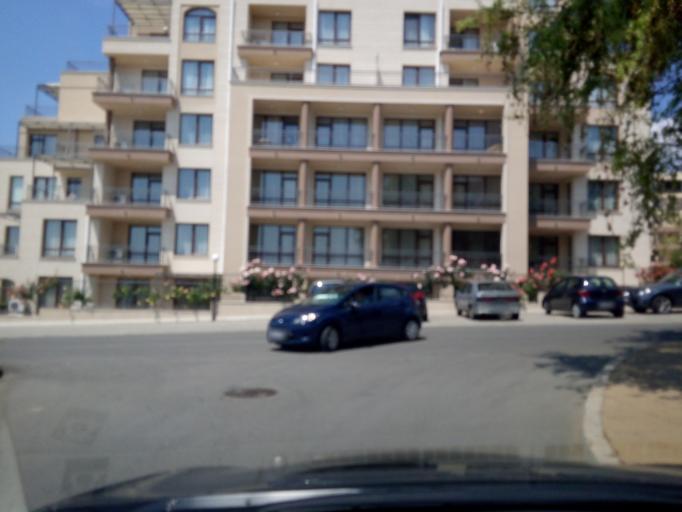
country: BG
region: Burgas
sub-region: Obshtina Nesebur
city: Sveti Vlas
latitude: 42.7119
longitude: 27.7458
